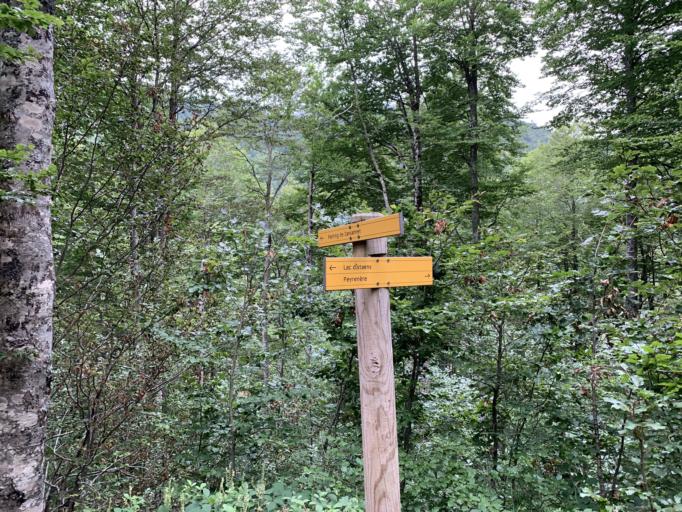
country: ES
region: Aragon
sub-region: Provincia de Huesca
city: Canfranc
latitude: 42.7989
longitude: -0.5579
